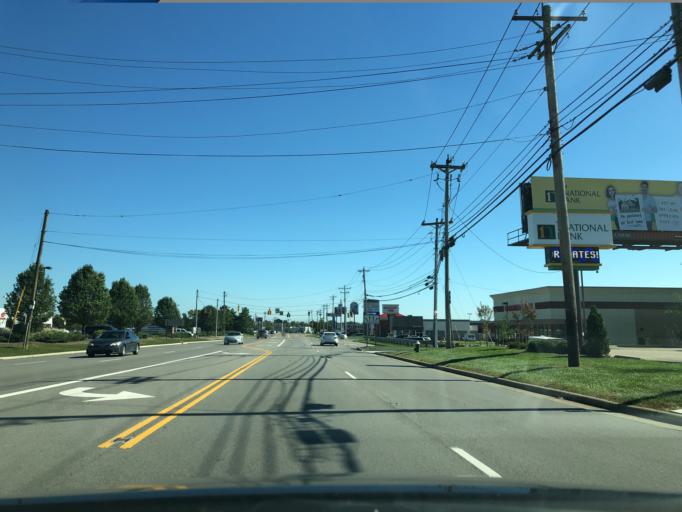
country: US
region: Ohio
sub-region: Hamilton County
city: Sixteen Mile Stand
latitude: 39.2926
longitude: -84.3127
